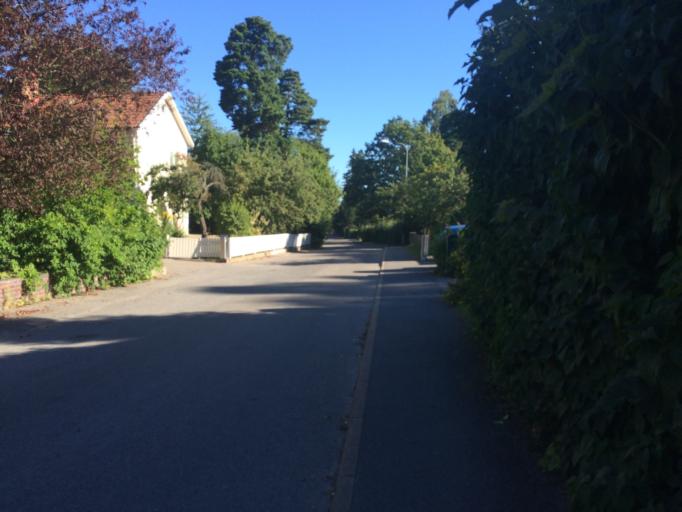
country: SE
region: Stockholm
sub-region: Stockholms Kommun
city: Kista
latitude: 59.3763
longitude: 17.8887
